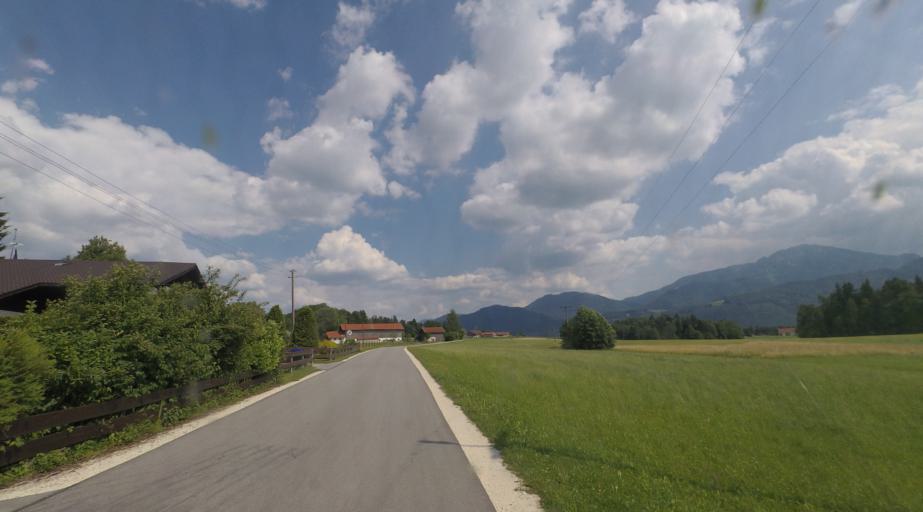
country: DE
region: Bavaria
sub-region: Upper Bavaria
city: Grabenstatt
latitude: 47.8251
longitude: 12.5499
